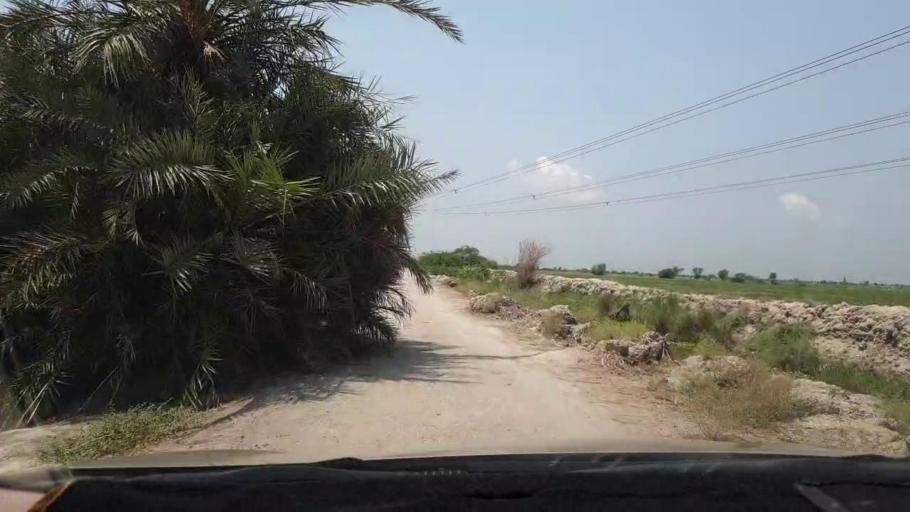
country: PK
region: Sindh
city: Naudero
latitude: 27.6647
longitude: 68.2779
